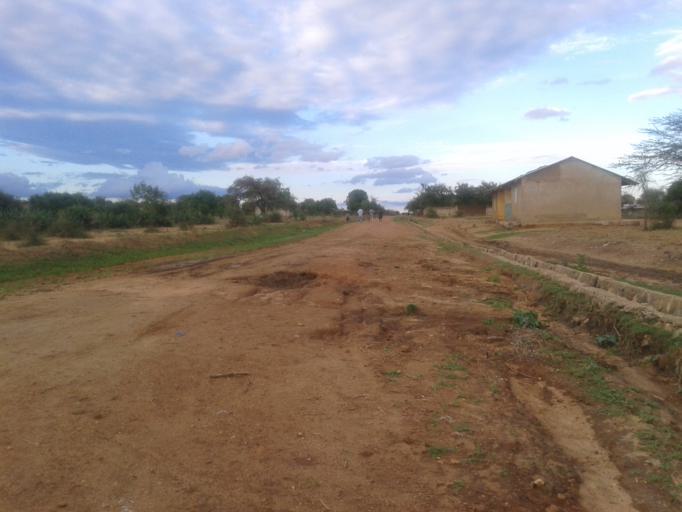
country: UG
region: Northern Region
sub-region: Kotido District
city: Kotido
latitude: 2.9947
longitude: 34.1055
